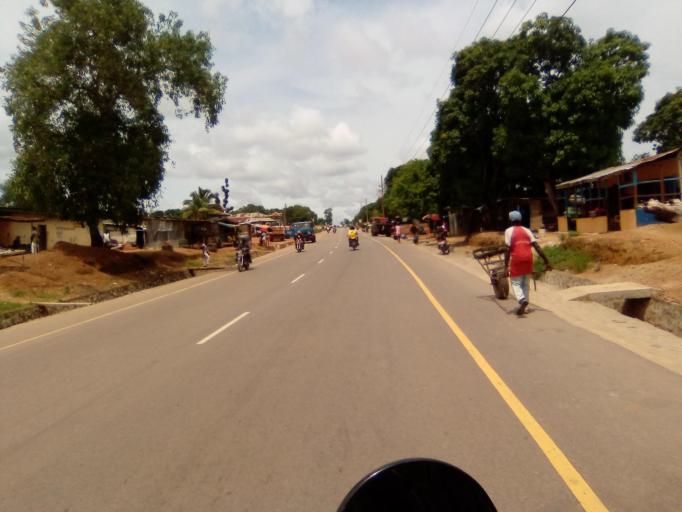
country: SL
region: Southern Province
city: Bo
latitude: 7.9352
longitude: -11.7256
